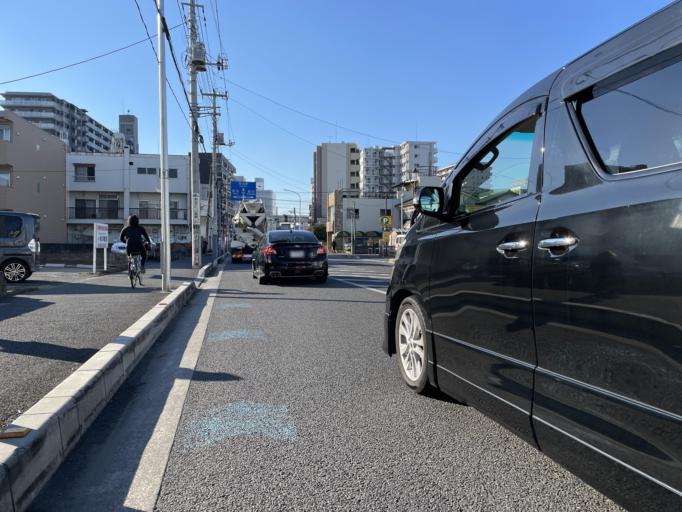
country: JP
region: Saitama
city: Soka
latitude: 35.8281
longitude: 139.8085
